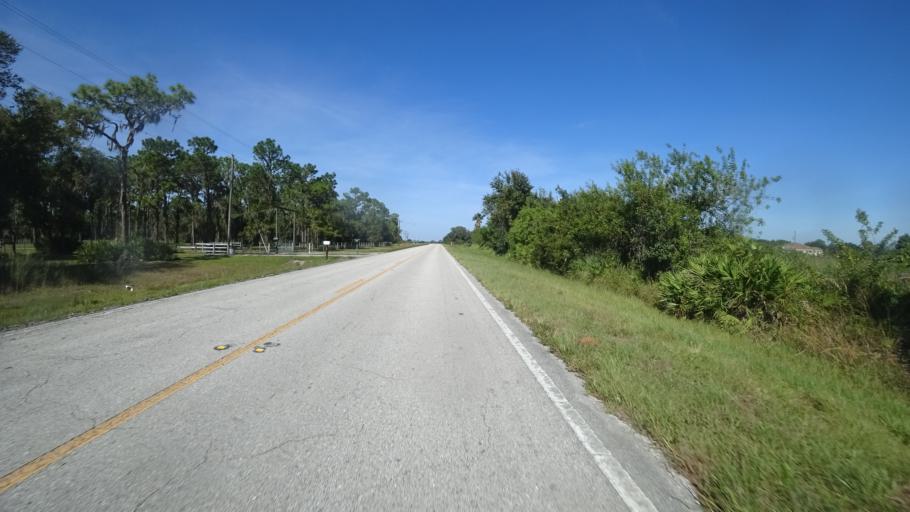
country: US
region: Florida
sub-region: Sarasota County
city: The Meadows
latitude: 27.4641
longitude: -82.3032
